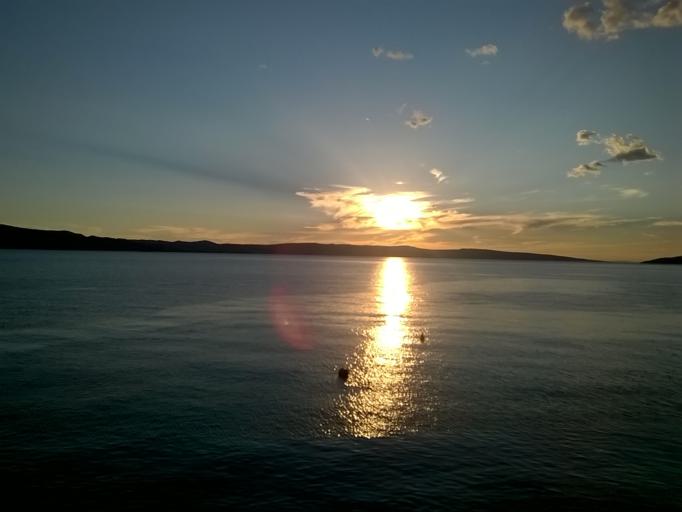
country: HR
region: Licko-Senjska
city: Karlobag
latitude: 44.5308
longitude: 15.0653
